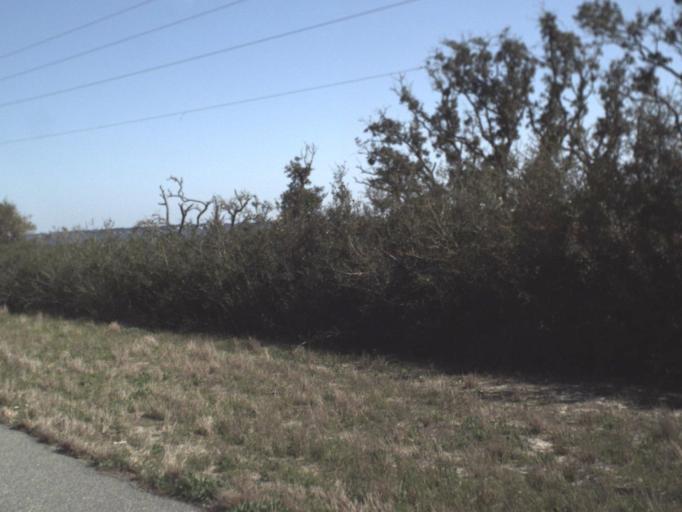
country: US
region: Florida
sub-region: Wakulla County
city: Crawfordville
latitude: 29.9245
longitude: -84.4159
